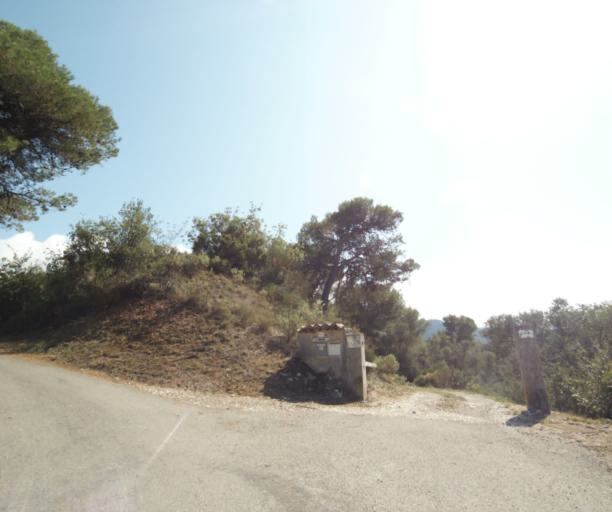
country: FR
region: Provence-Alpes-Cote d'Azur
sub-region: Departement des Alpes-Maritimes
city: Drap
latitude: 43.7559
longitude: 7.3421
